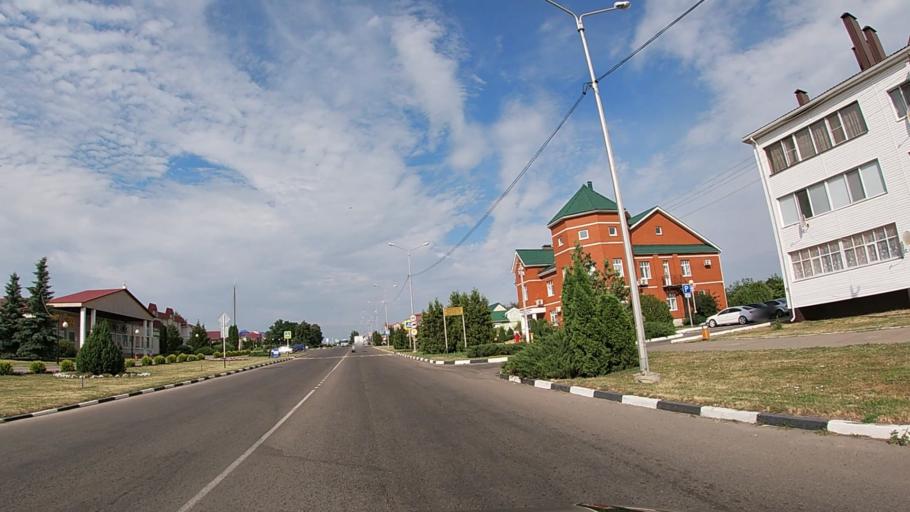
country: RU
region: Belgorod
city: Krasnaya Yaruga
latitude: 50.8025
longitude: 35.6590
